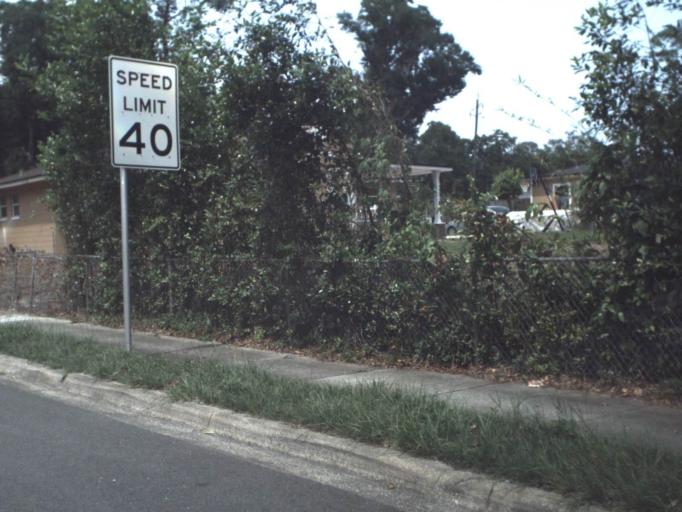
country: US
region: Florida
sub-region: Duval County
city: Jacksonville
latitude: 30.3030
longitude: -81.6009
